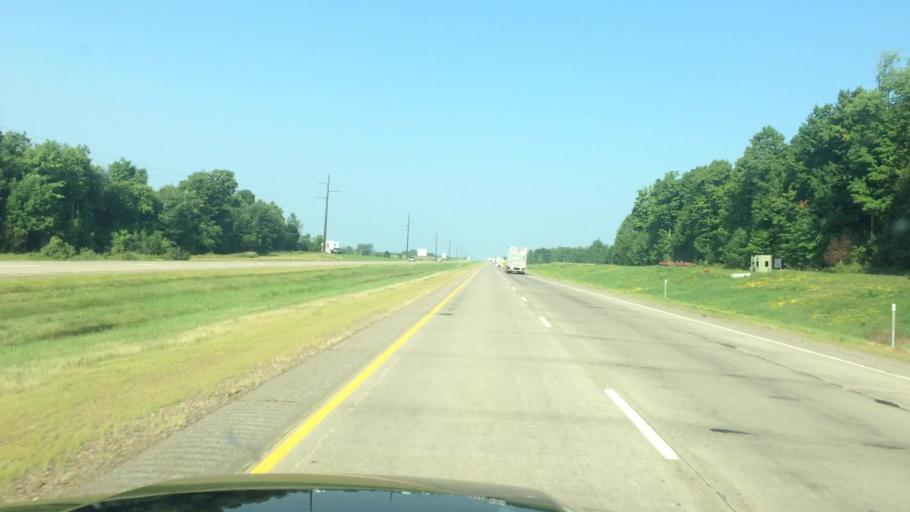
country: US
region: Wisconsin
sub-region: Marathon County
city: Edgar
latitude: 44.9445
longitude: -89.9704
